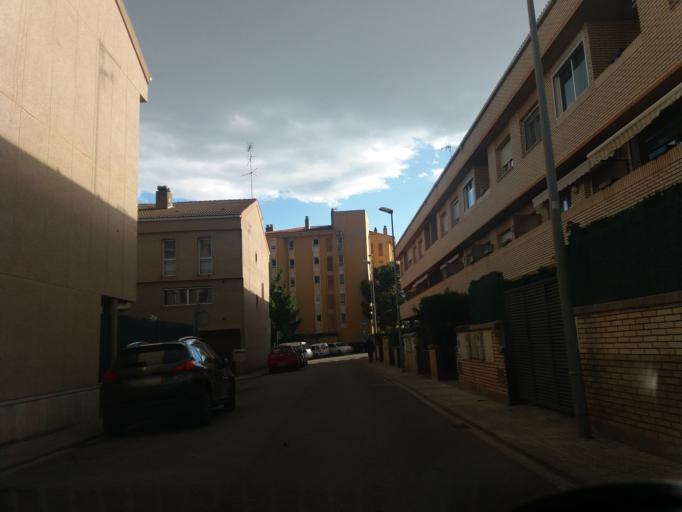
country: ES
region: Catalonia
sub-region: Provincia de Barcelona
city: Manresa
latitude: 41.7419
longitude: 1.8346
